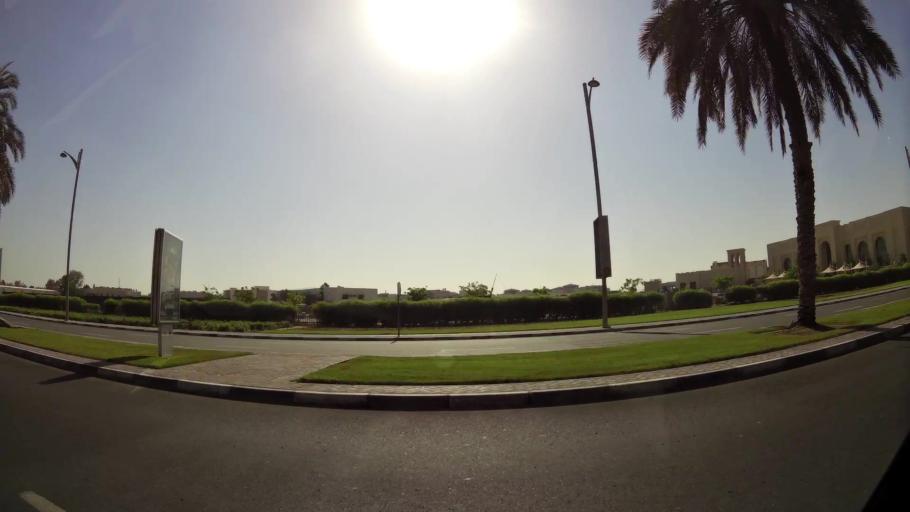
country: AE
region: Dubai
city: Dubai
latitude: 25.1348
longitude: 55.1881
